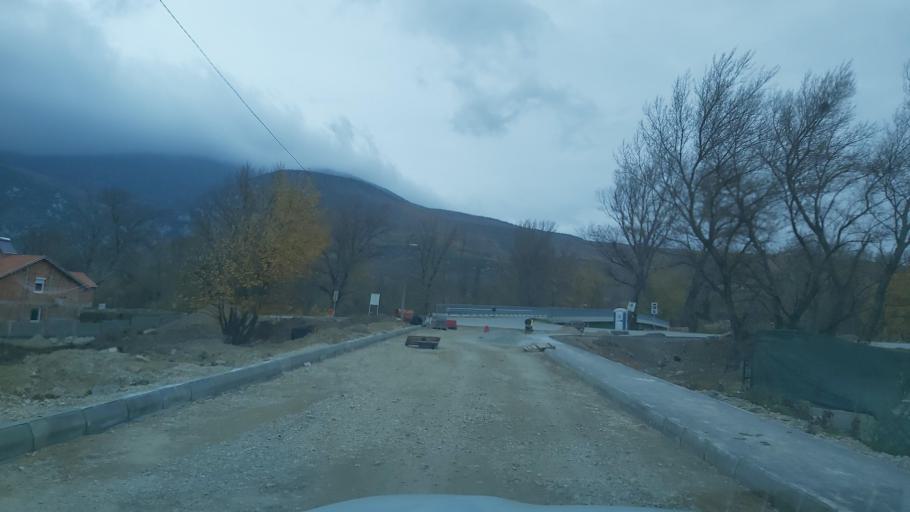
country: MK
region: Demir Kapija
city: Demir Kapija
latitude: 41.4072
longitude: 22.2428
